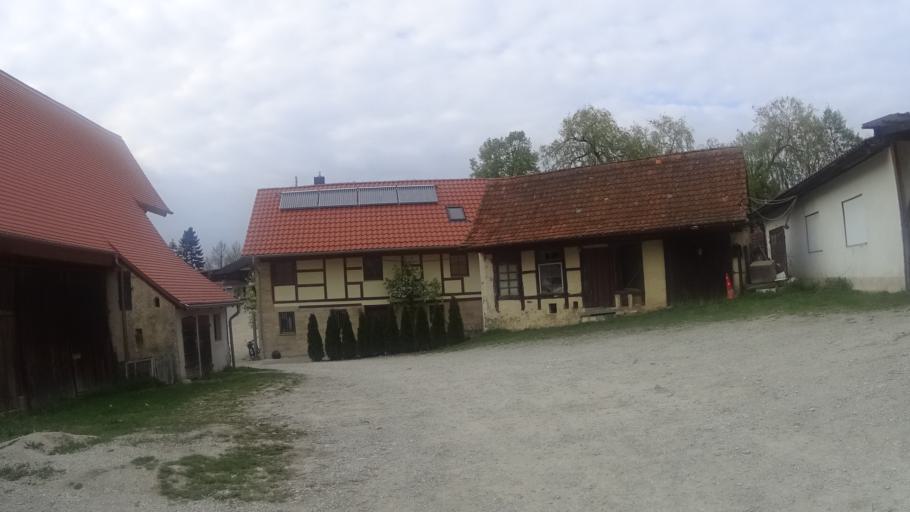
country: DE
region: Bavaria
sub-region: Upper Franconia
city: Kleinsendelbach
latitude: 49.5970
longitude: 11.1860
